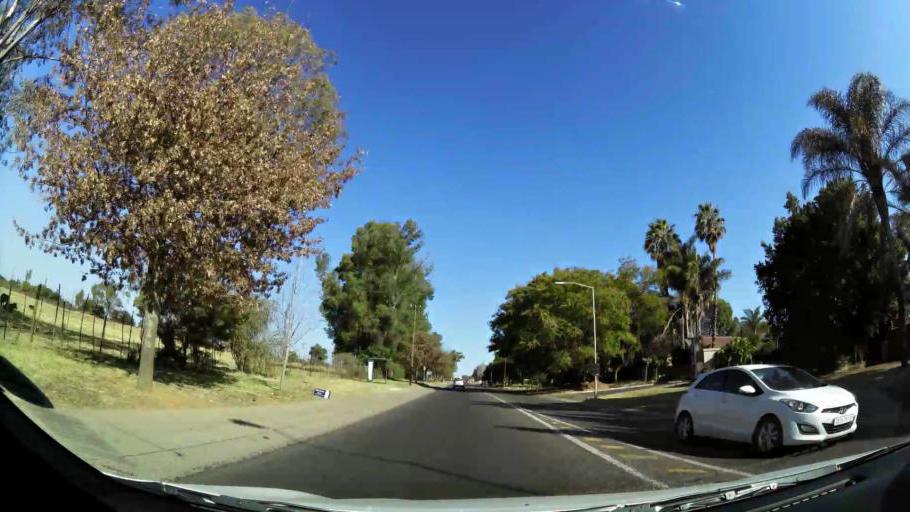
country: ZA
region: Gauteng
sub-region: City of Tshwane Metropolitan Municipality
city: Centurion
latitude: -25.8247
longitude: 28.2952
